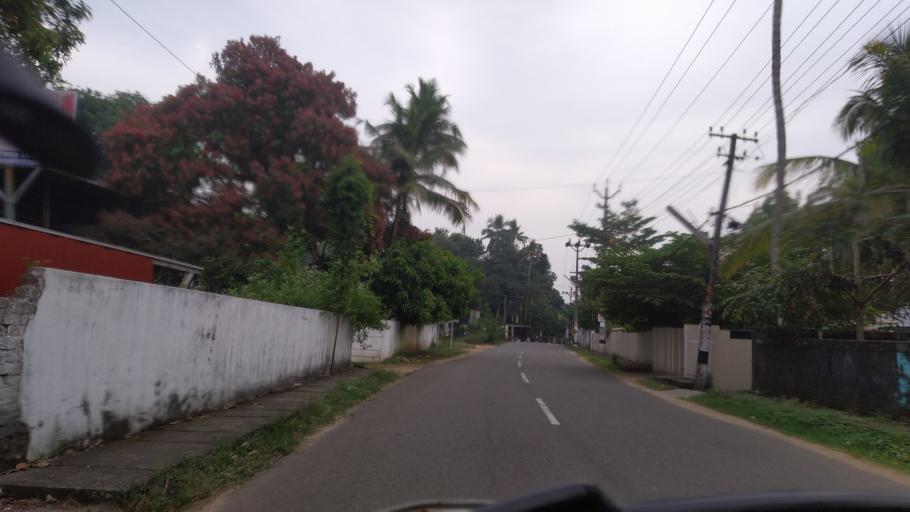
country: IN
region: Kerala
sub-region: Ernakulam
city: Elur
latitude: 10.1357
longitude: 76.2476
